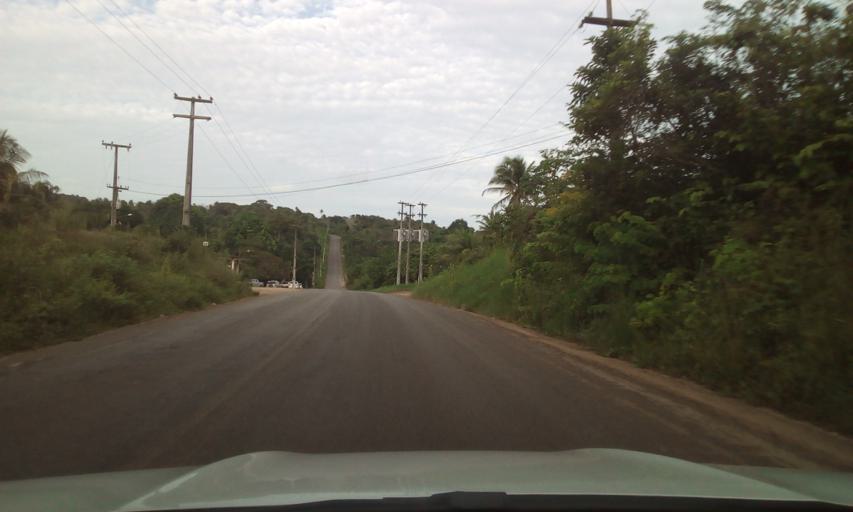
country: BR
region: Paraiba
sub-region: Conde
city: Conde
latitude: -7.2720
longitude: -34.8927
